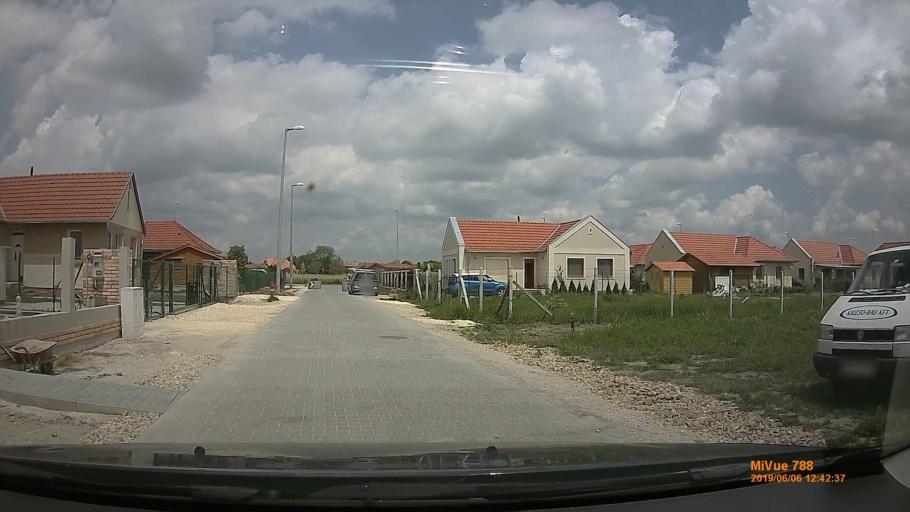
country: HU
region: Pest
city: Budakalasz
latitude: 47.6241
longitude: 19.0536
